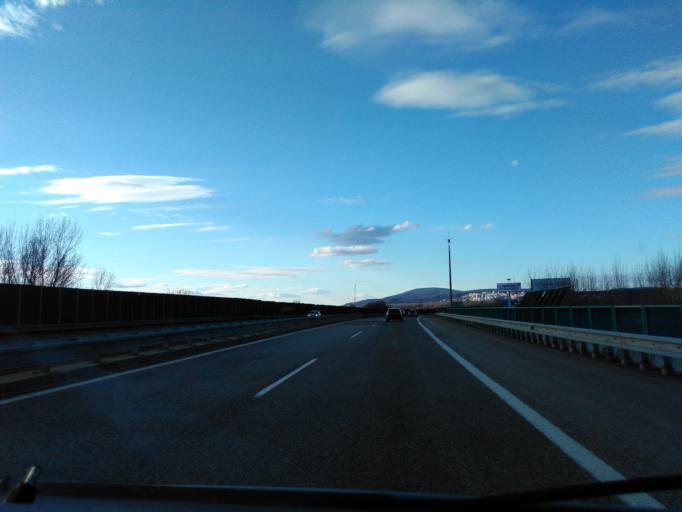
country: AT
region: Burgenland
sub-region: Politischer Bezirk Neusiedl am See
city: Kittsee
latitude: 48.1074
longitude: 17.0884
